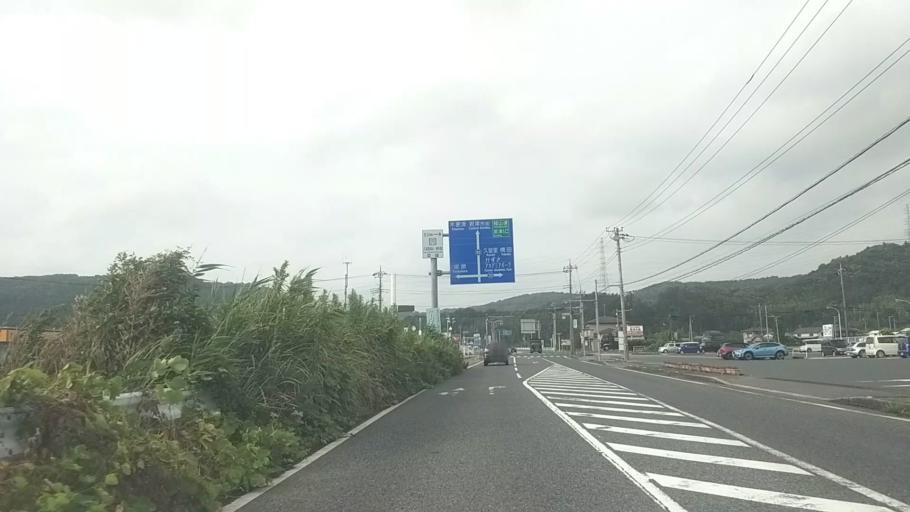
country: JP
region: Chiba
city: Kisarazu
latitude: 35.3016
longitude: 139.9869
